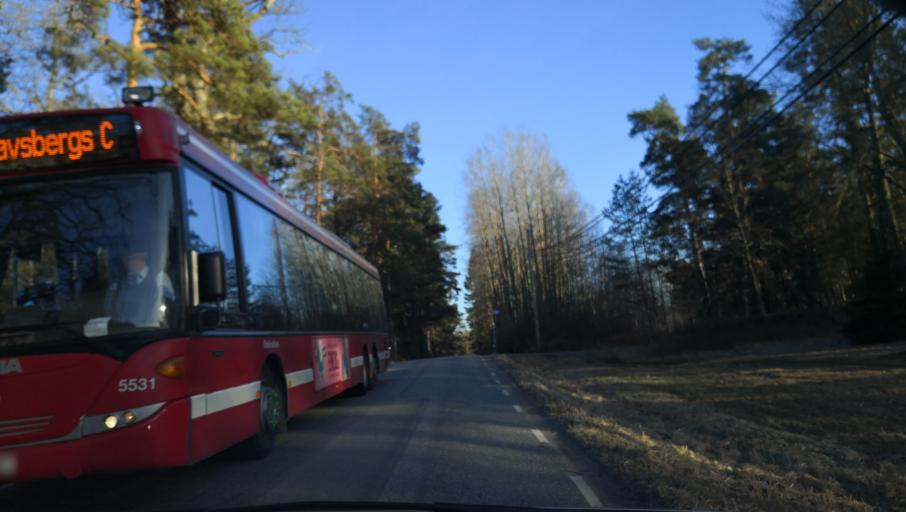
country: SE
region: Stockholm
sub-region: Varmdo Kommun
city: Gustavsberg
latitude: 59.3293
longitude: 18.4111
